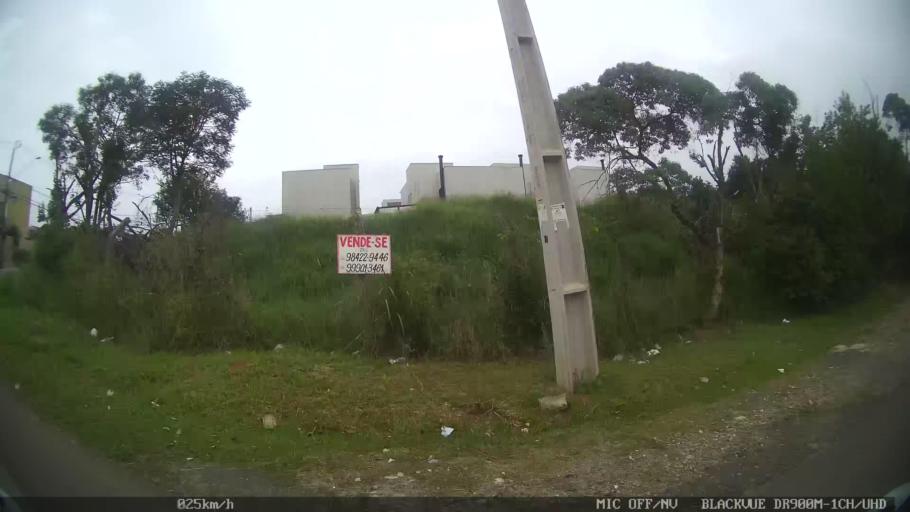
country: BR
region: Parana
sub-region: Almirante Tamandare
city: Almirante Tamandare
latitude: -25.3760
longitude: -49.3274
